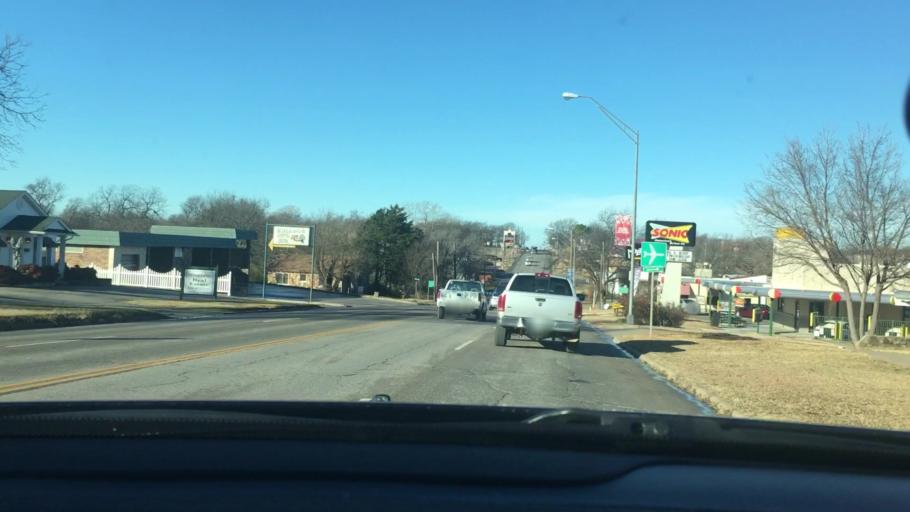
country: US
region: Oklahoma
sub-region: Murray County
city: Sulphur
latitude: 34.5065
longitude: -96.9838
